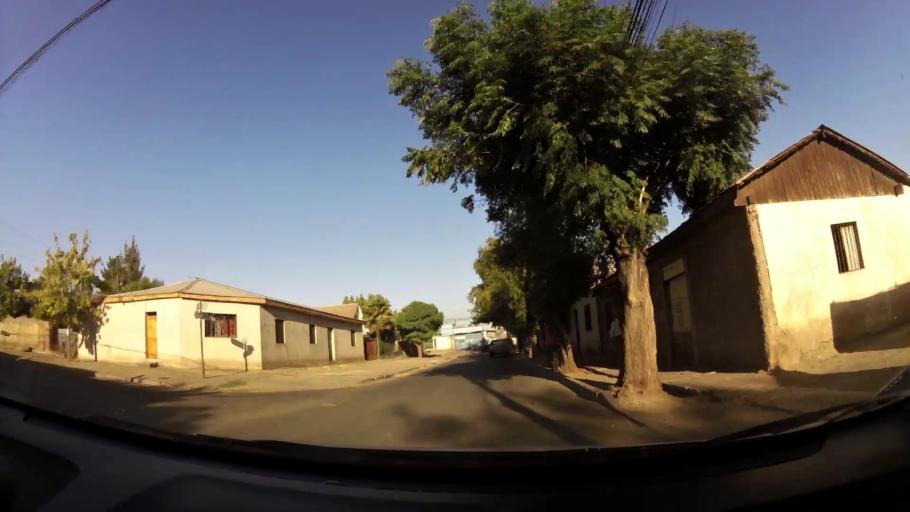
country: CL
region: Maule
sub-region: Provincia de Talca
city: Talca
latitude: -35.4394
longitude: -71.6476
